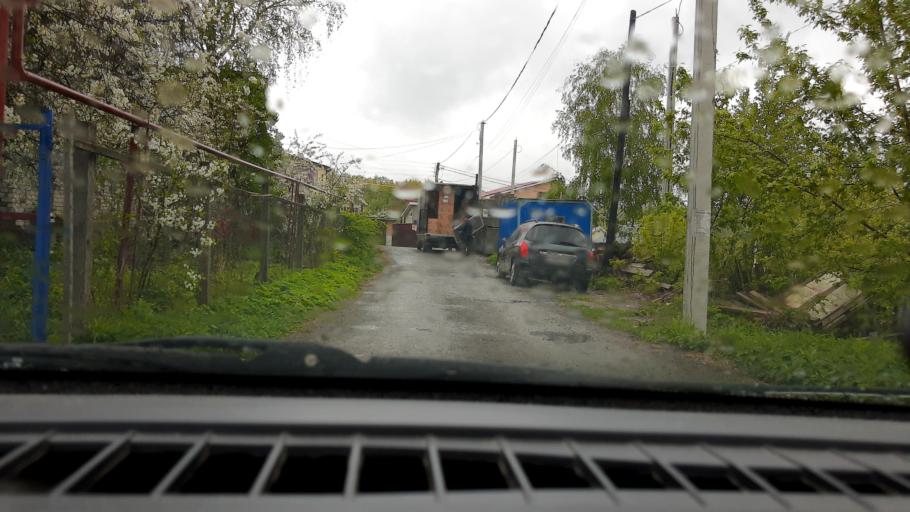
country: RU
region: Nizjnij Novgorod
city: Nizhniy Novgorod
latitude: 56.2779
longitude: 44.0254
